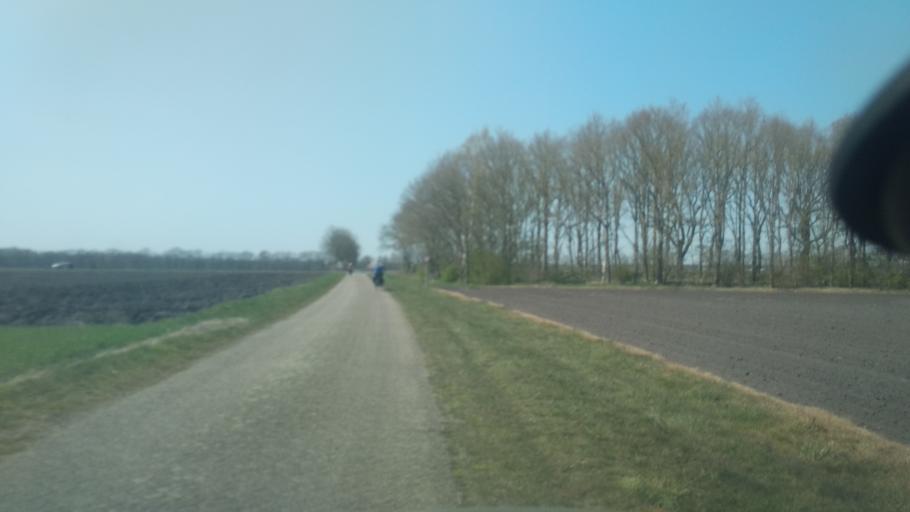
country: NL
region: Drenthe
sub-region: Gemeente Borger-Odoorn
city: Borger
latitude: 52.9106
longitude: 6.7561
